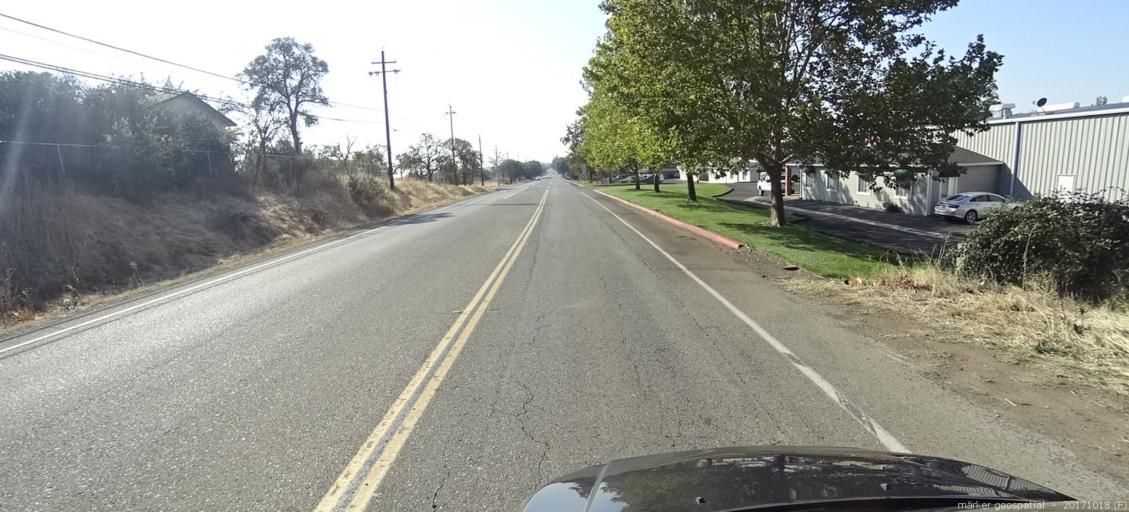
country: US
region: California
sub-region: Shasta County
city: Palo Cedro
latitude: 40.5484
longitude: -122.3028
